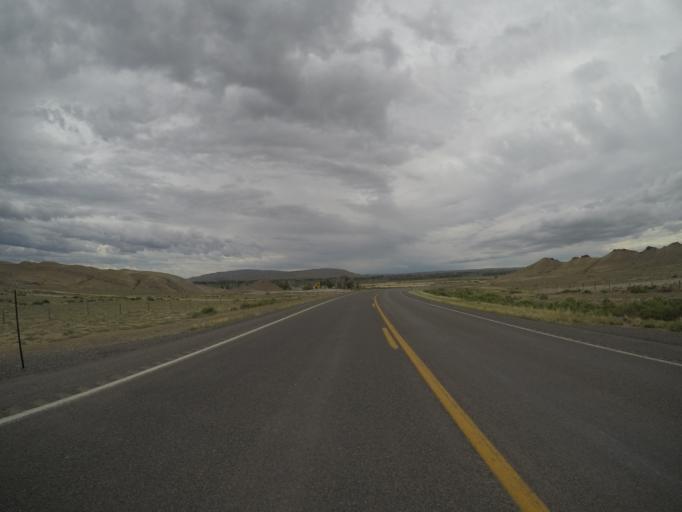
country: US
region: Wyoming
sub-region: Big Horn County
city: Lovell
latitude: 44.8810
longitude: -108.2895
